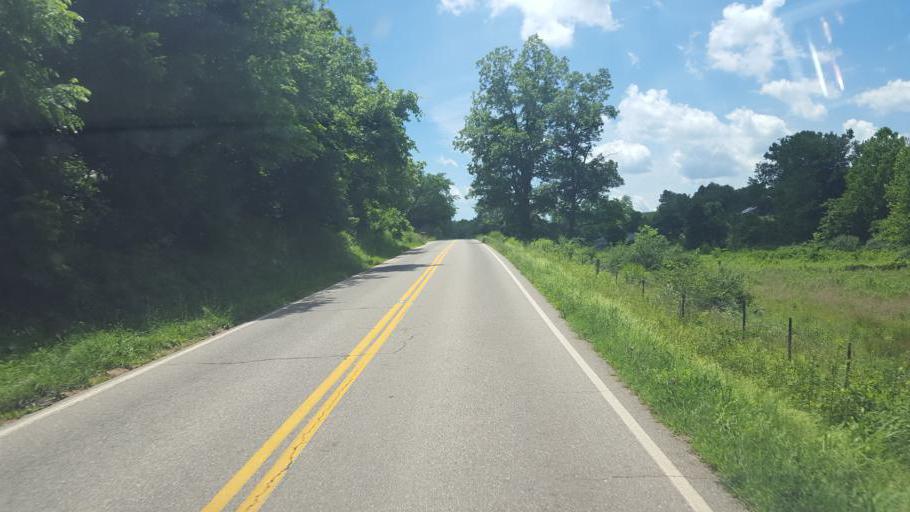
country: US
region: Ohio
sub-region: Gallia County
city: Gallipolis
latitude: 38.7380
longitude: -82.3687
